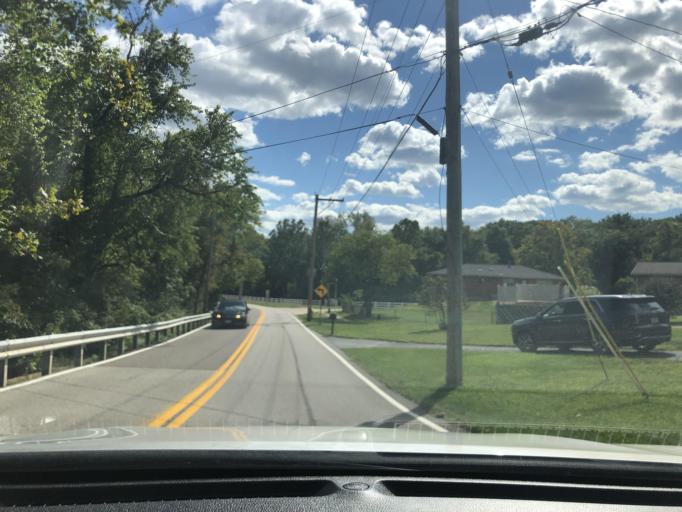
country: US
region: Missouri
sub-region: Saint Louis County
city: Green Park
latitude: 38.5018
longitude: -90.3488
